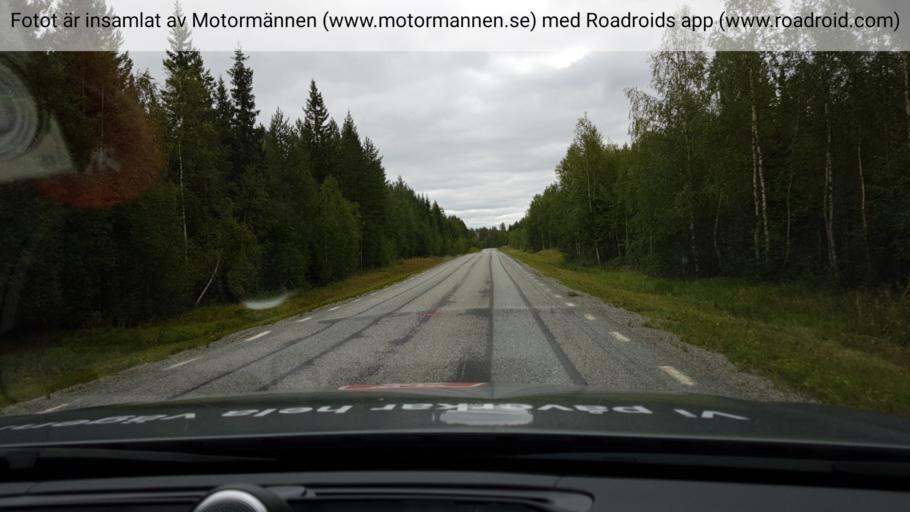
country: SE
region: Jaemtland
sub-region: Stroemsunds Kommun
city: Stroemsund
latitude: 63.8734
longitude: 15.8514
